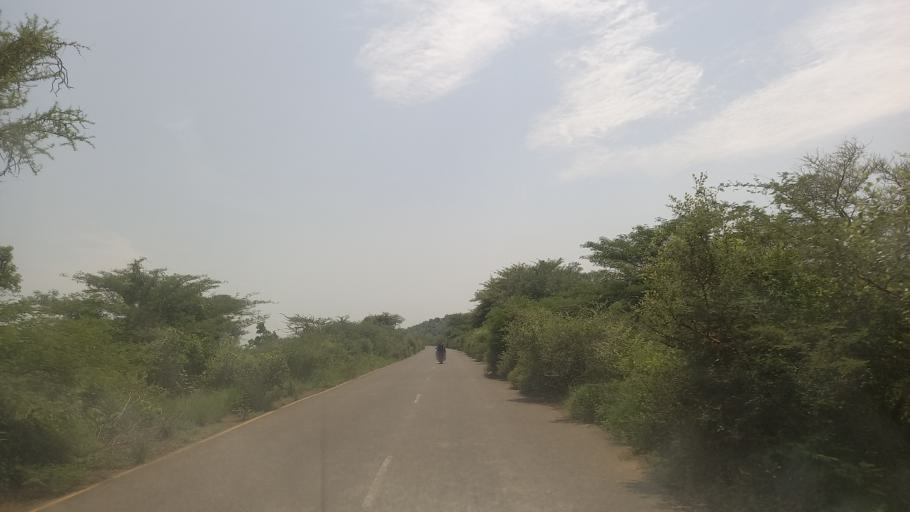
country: ET
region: Gambela
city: Gambela
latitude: 8.2820
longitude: 34.2213
